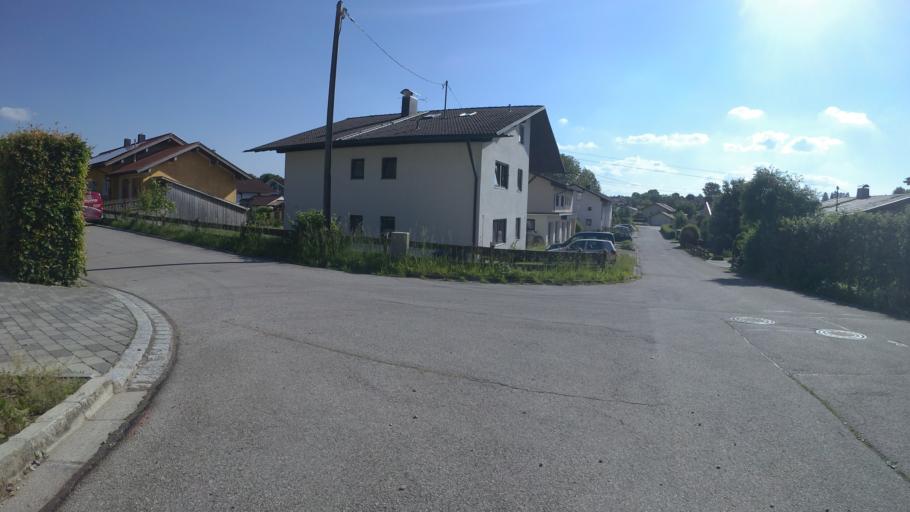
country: DE
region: Bavaria
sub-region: Upper Bavaria
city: Seeon-Seebruck
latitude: 47.9568
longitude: 12.5034
